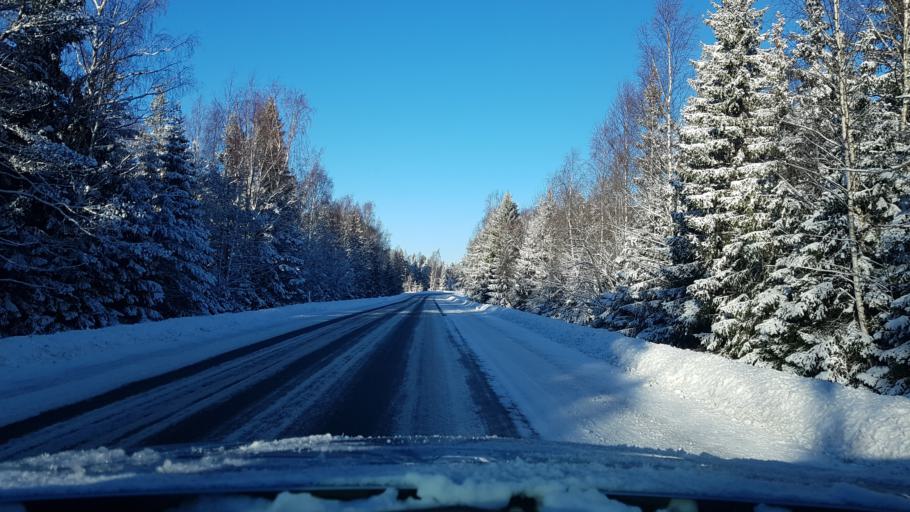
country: EE
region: Hiiumaa
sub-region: Kaerdla linn
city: Kardla
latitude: 58.9768
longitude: 22.8152
